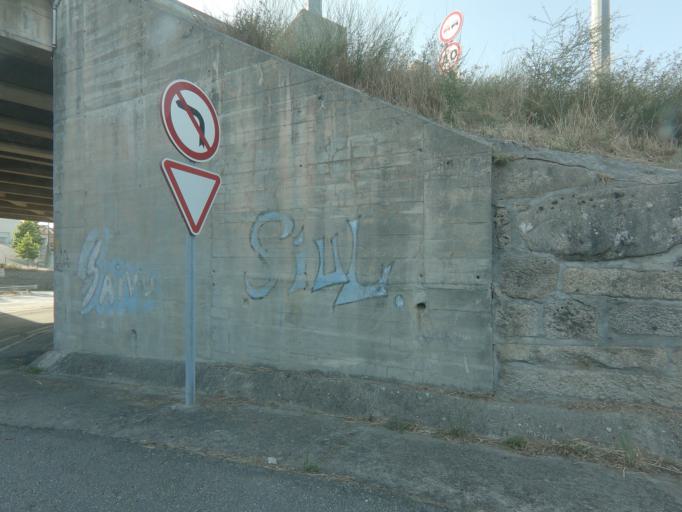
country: PT
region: Vila Real
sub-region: Vila Real
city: Vila Real
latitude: 41.2838
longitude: -7.7596
